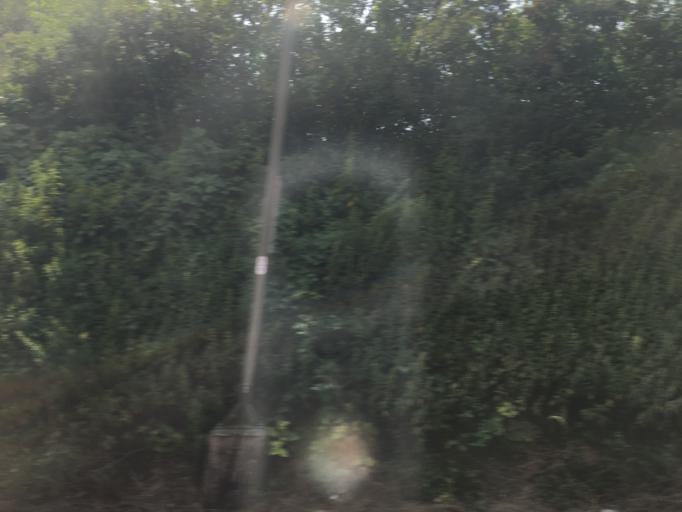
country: DE
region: Hesse
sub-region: Regierungsbezirk Darmstadt
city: Steinbach am Taunus
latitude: 50.1628
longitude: 8.5888
